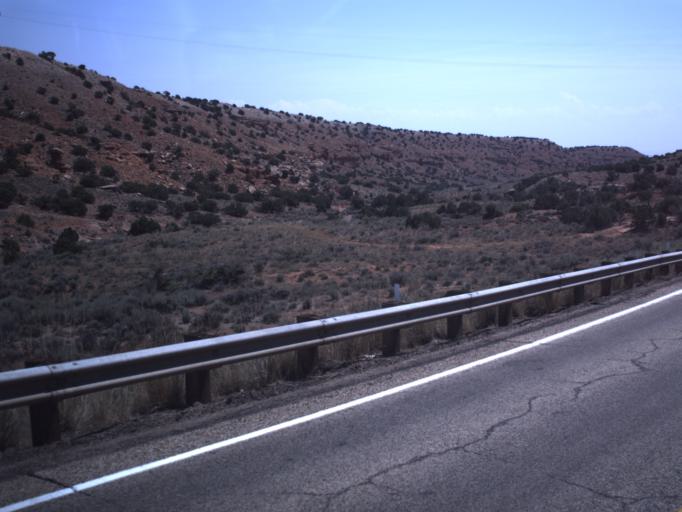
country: US
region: Utah
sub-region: Uintah County
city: Maeser
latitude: 40.4259
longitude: -109.6683
